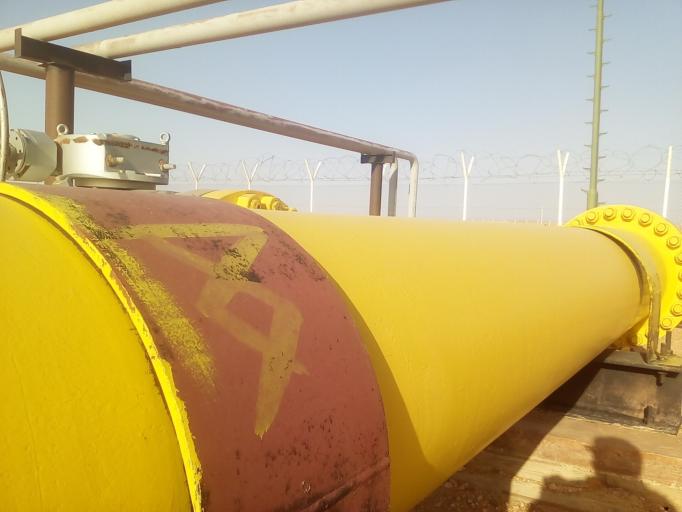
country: DZ
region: Ghardaia
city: Ghardaia
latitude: 32.5576
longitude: 3.1653
